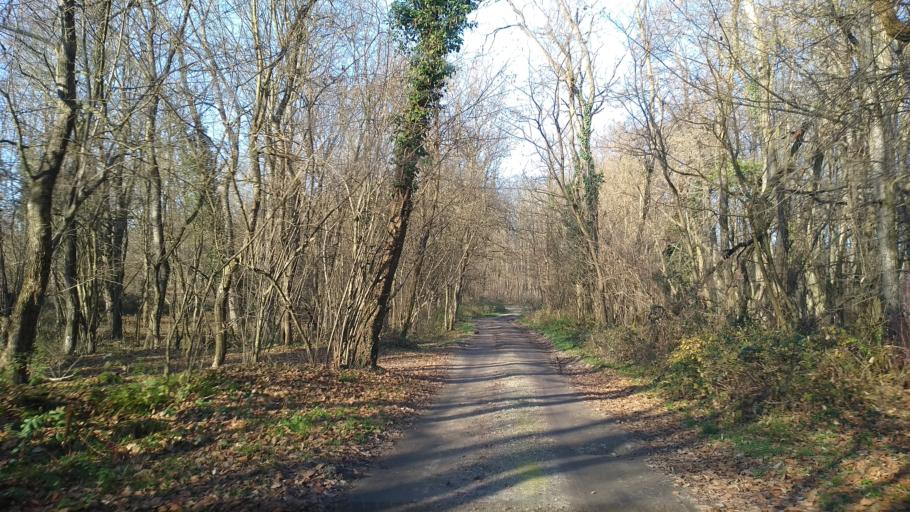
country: HU
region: Somogy
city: Barcs
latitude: 45.9511
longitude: 17.5212
